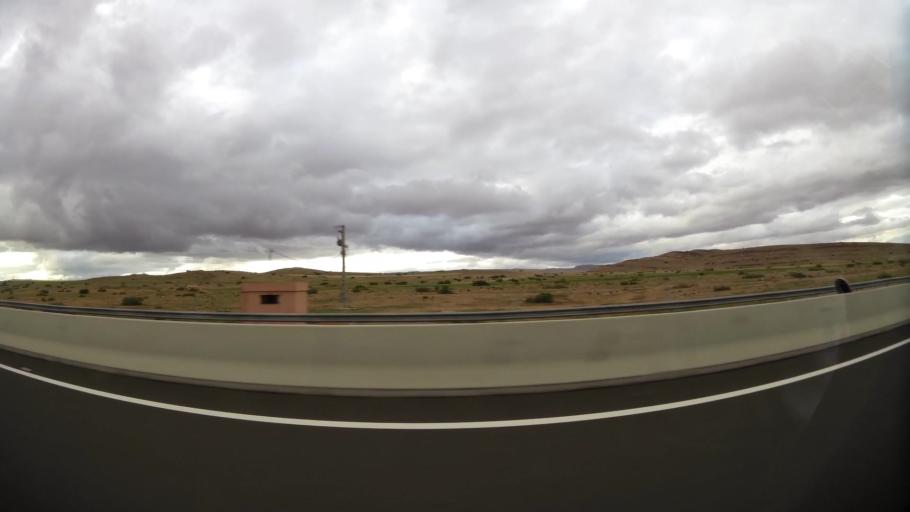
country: MA
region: Taza-Al Hoceima-Taounate
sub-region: Taza
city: Taza
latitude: 34.3073
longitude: -3.6907
